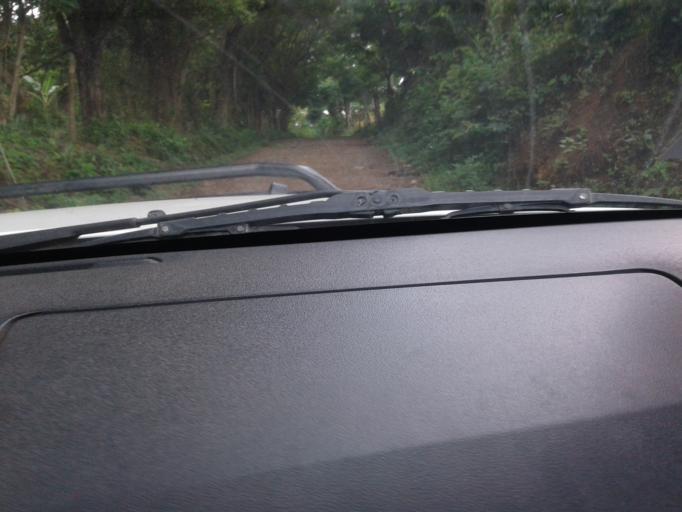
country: NI
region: Matagalpa
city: San Ramon
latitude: 12.9104
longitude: -85.7341
